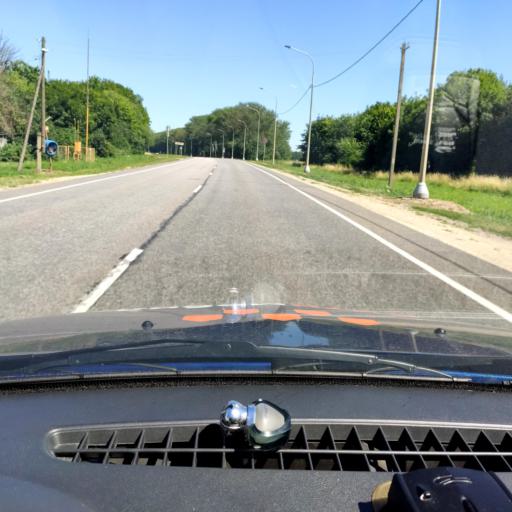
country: RU
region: Orjol
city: Pokrovskoye
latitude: 52.6195
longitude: 36.7420
